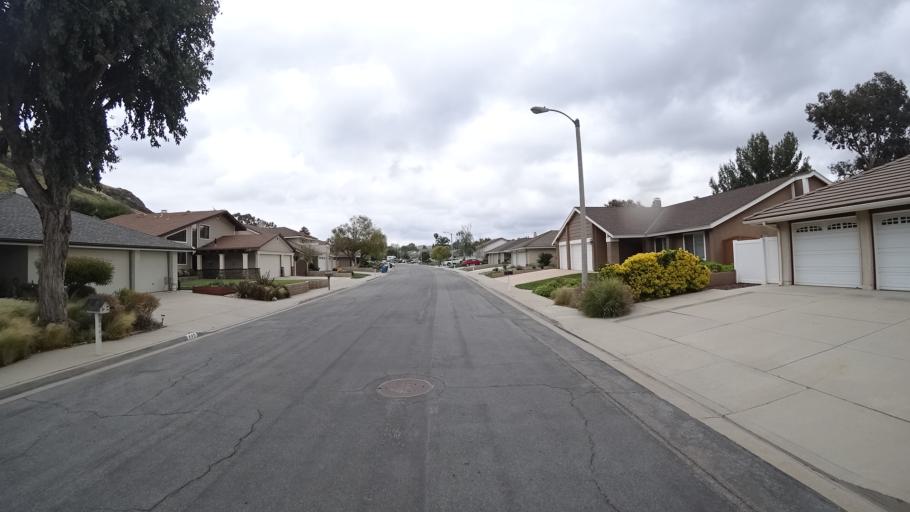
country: US
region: California
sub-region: Ventura County
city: Moorpark
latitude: 34.2241
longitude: -118.8891
